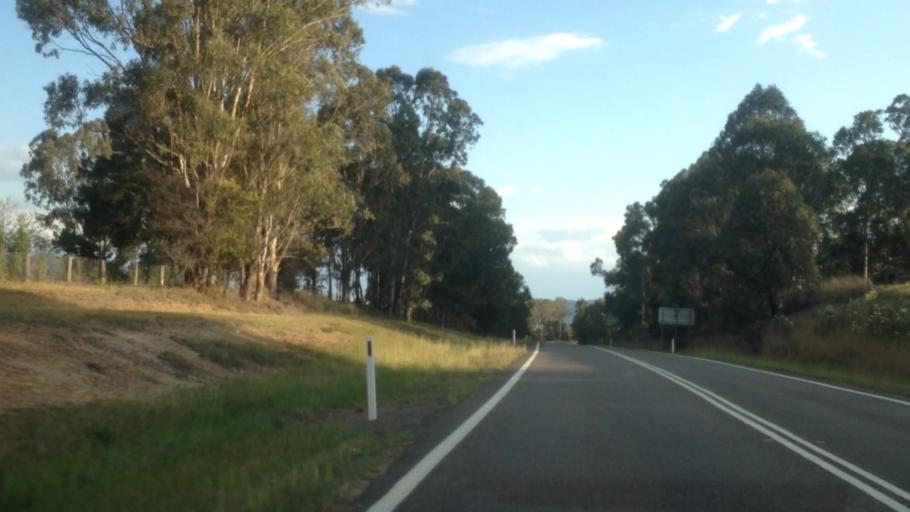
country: AU
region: New South Wales
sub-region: Cessnock
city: Kurri Kurri
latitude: -32.8661
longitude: 151.4800
